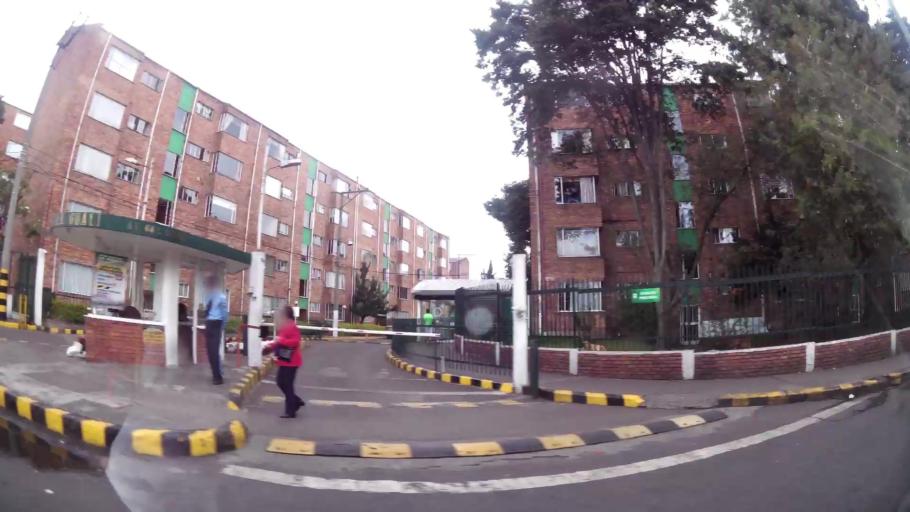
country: CO
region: Bogota D.C.
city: Bogota
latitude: 4.6711
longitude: -74.0934
